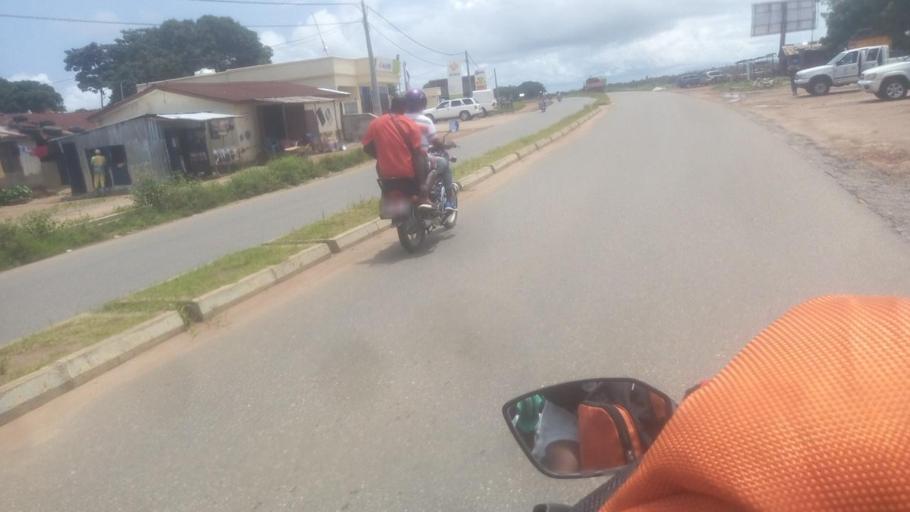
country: SL
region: Northern Province
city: Masoyila
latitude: 8.6119
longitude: -13.1893
